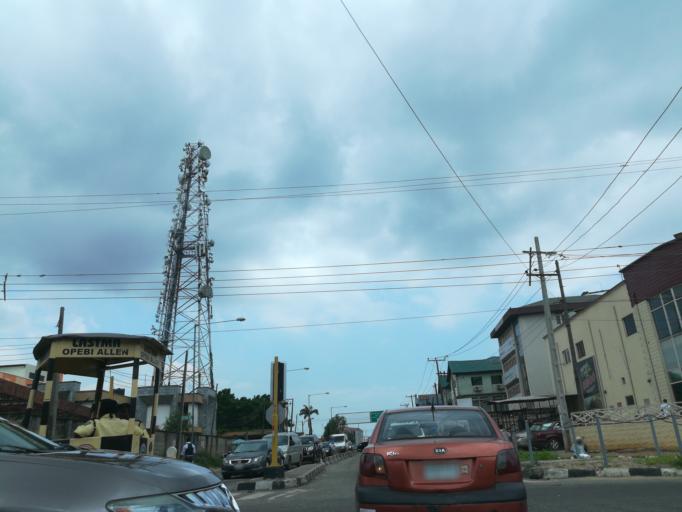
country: NG
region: Lagos
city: Ikeja
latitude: 6.5916
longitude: 3.3594
